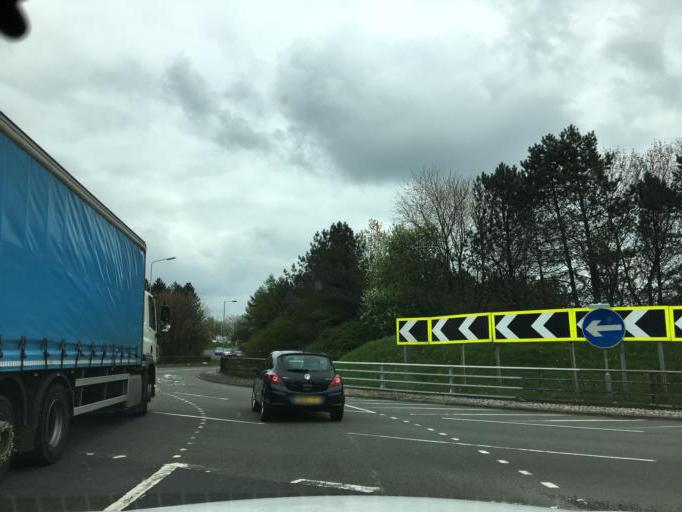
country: GB
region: Wales
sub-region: Carmarthenshire
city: Cross Hands
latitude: 51.7971
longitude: -4.0839
